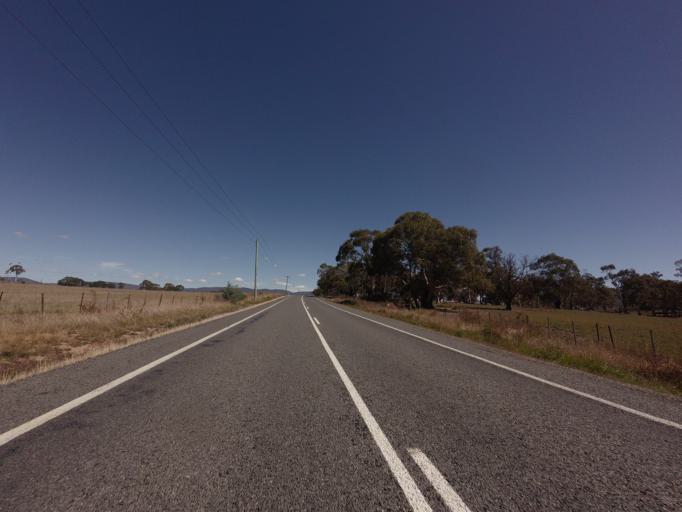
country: AU
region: Tasmania
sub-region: Northern Midlands
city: Evandale
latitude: -41.7612
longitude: 147.7504
